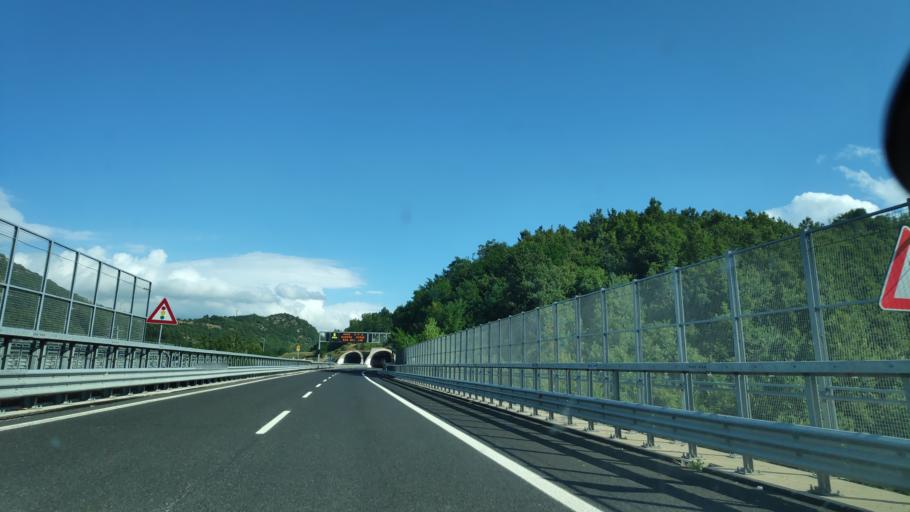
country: IT
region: Campania
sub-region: Provincia di Salerno
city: Casalbuono
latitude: 40.2304
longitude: 15.6675
